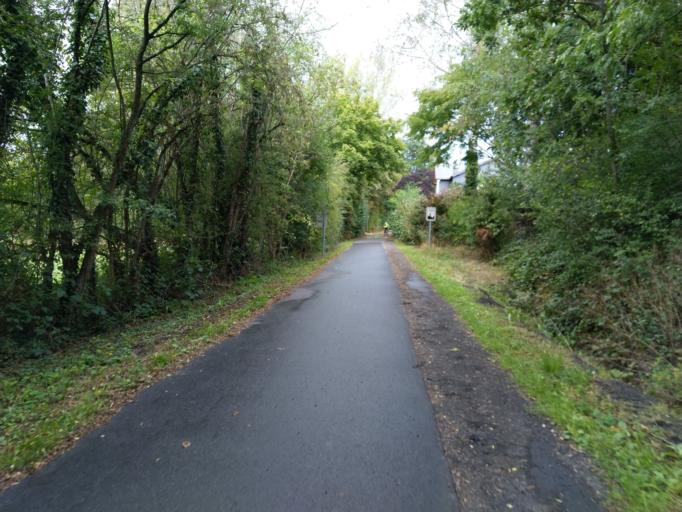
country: BE
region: Wallonia
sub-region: Province de Liege
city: Aubel
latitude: 50.6900
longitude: 5.8552
